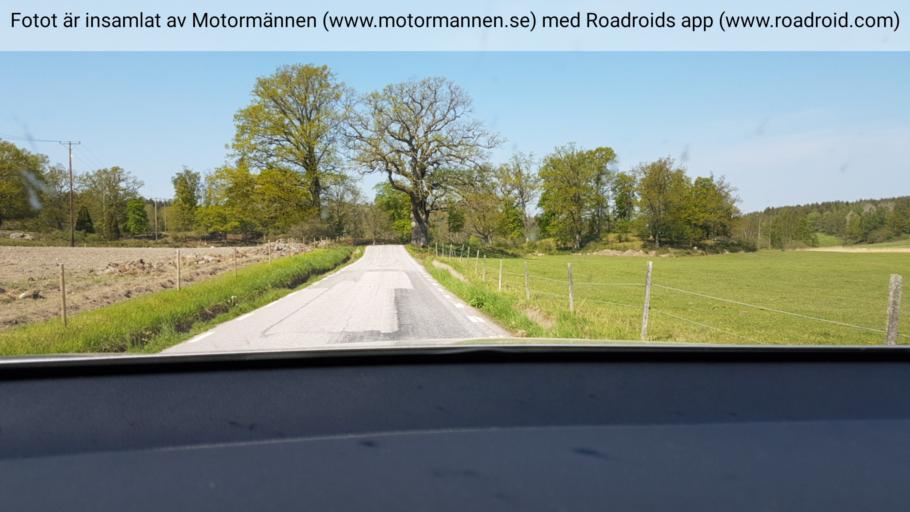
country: SE
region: Kalmar
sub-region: Vasterviks Kommun
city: Forserum
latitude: 57.8526
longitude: 16.5252
